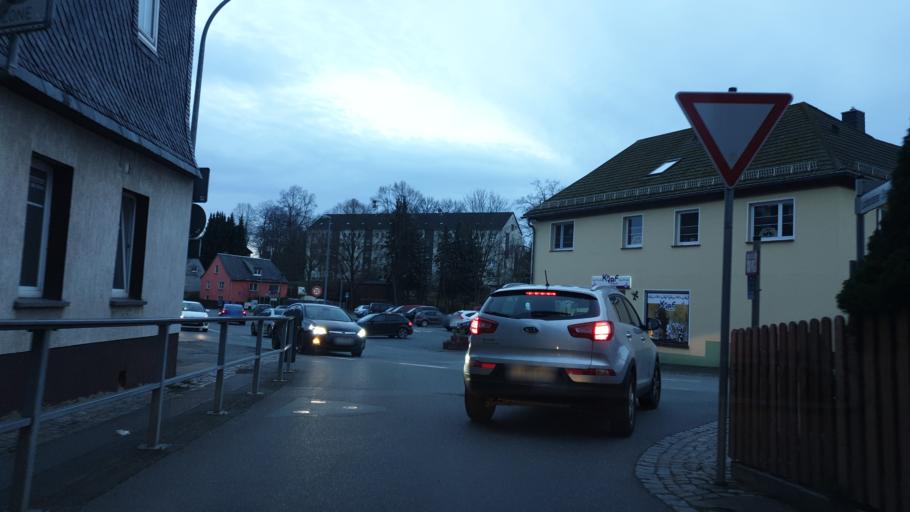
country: DE
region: Saxony
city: Hartenstein
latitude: 50.6638
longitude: 12.6669
